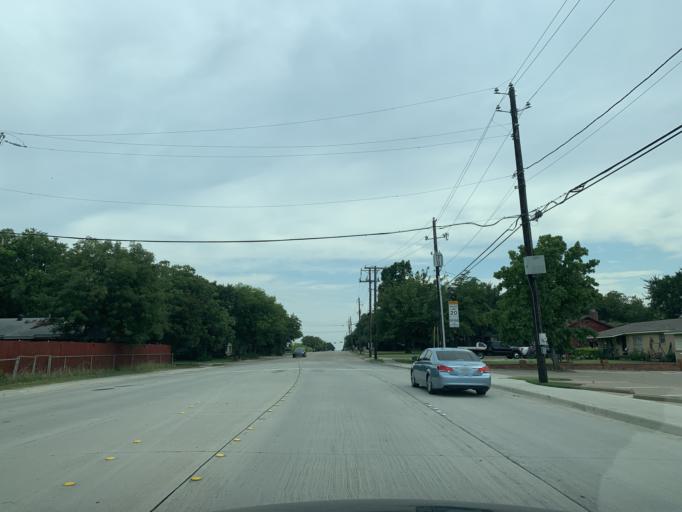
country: US
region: Texas
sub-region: Tarrant County
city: North Richland Hills
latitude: 32.8377
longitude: -97.2388
